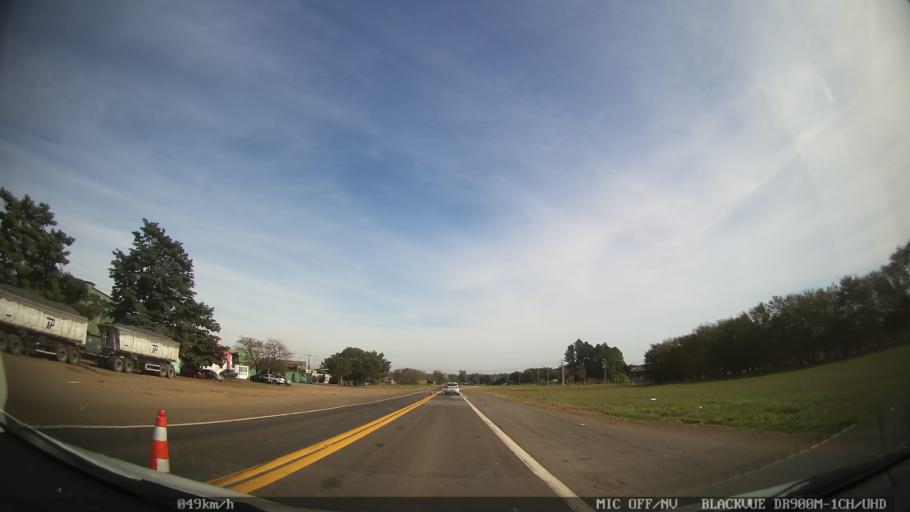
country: BR
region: Sao Paulo
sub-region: Rio Das Pedras
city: Rio das Pedras
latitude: -22.7943
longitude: -47.6173
